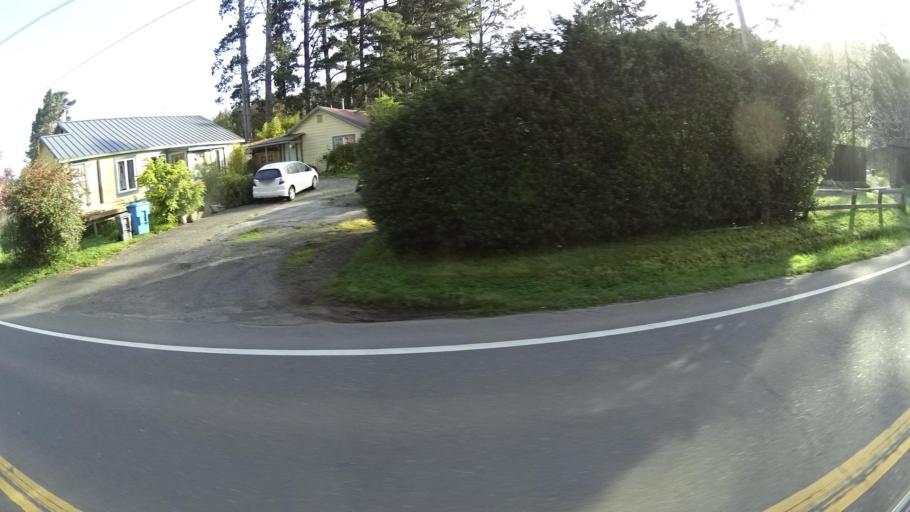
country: US
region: California
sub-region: Humboldt County
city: Myrtletown
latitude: 40.7692
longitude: -124.0711
